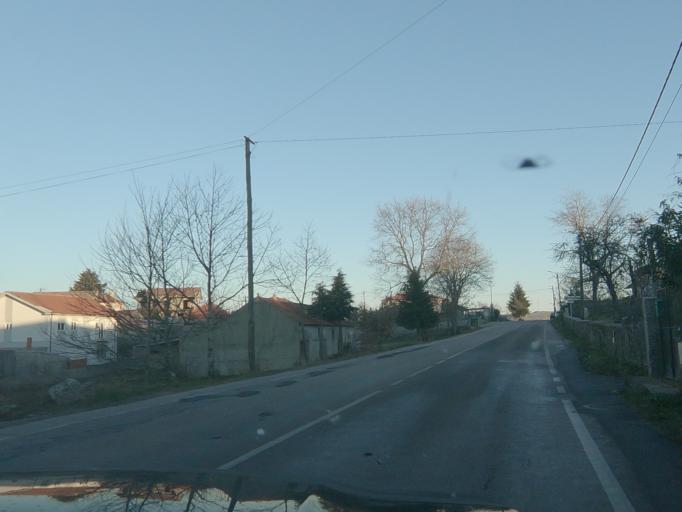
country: PT
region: Vila Real
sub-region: Vila Pouca de Aguiar
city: Vila Pouca de Aguiar
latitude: 41.5018
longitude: -7.6896
